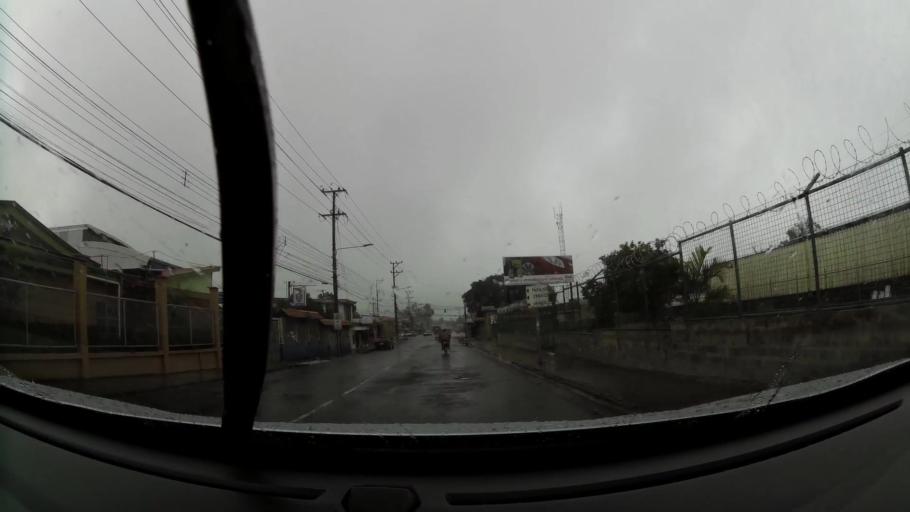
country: CR
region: Cartago
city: Cartago
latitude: 9.8620
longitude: -83.9133
